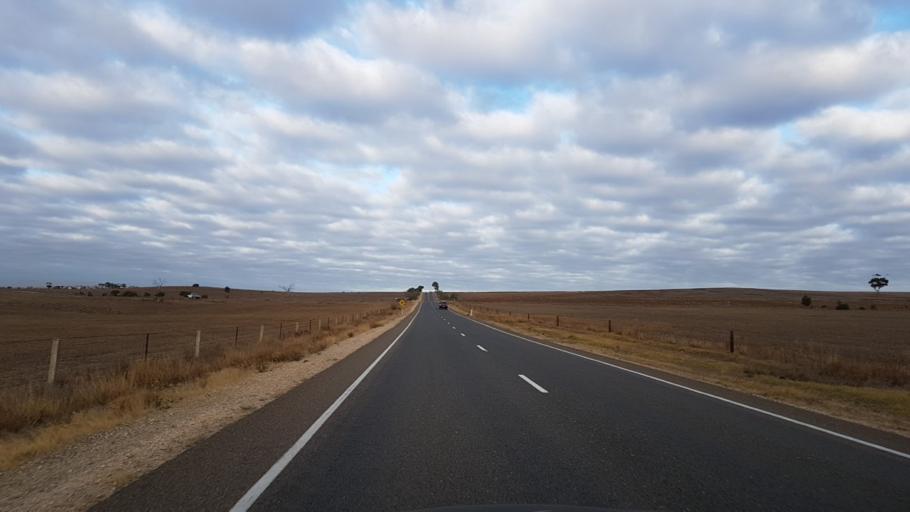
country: AU
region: South Australia
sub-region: Mount Barker
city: Callington
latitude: -35.1884
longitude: 138.9954
